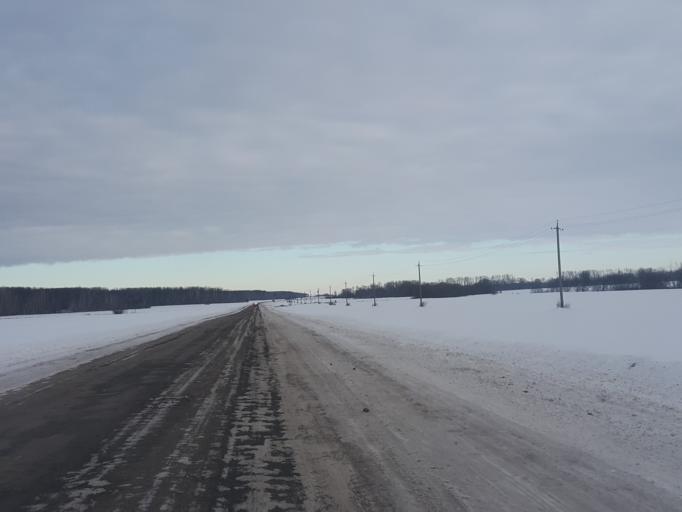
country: RU
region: Tambov
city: Novaya Lyada
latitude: 52.7405
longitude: 41.7030
